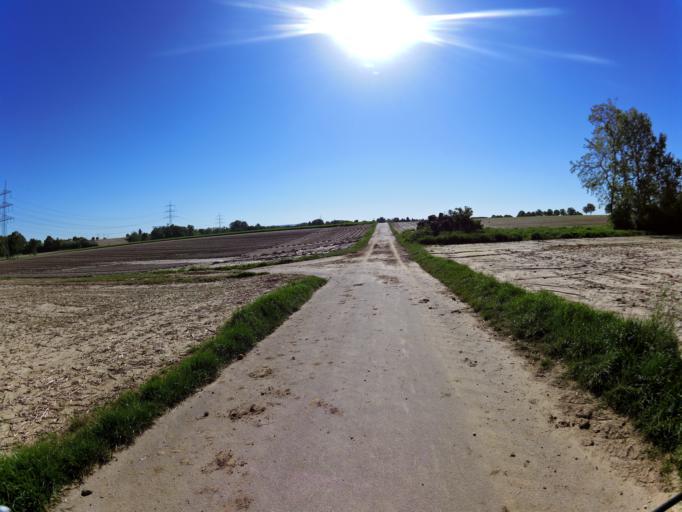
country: DE
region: North Rhine-Westphalia
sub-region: Regierungsbezirk Koln
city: Aldenhoven
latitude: 50.9359
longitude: 6.2811
